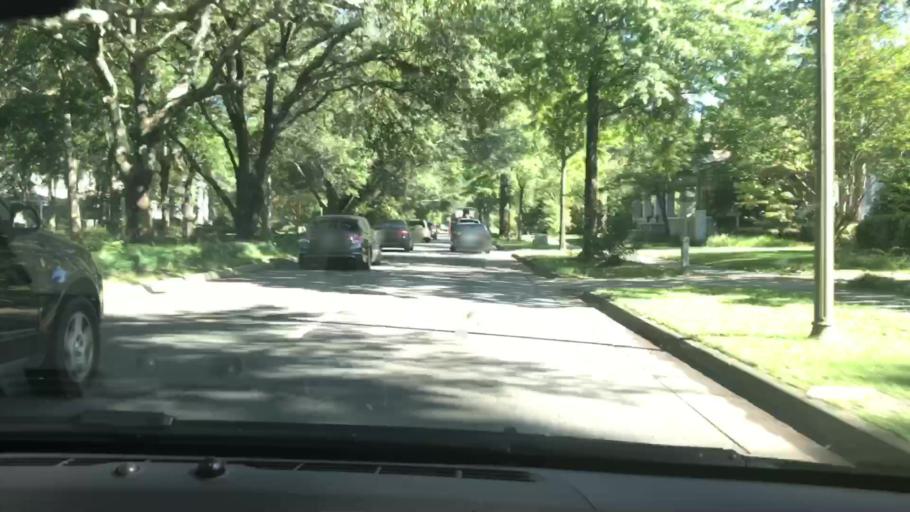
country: US
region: Alabama
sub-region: Barbour County
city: Eufaula
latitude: 31.8998
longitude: -85.1458
